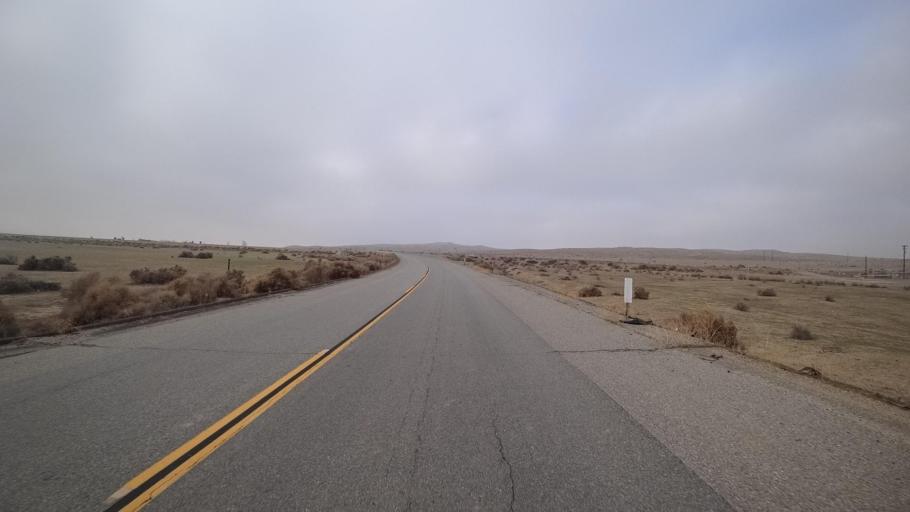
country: US
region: California
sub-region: Kern County
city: Maricopa
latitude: 35.1280
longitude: -119.3657
